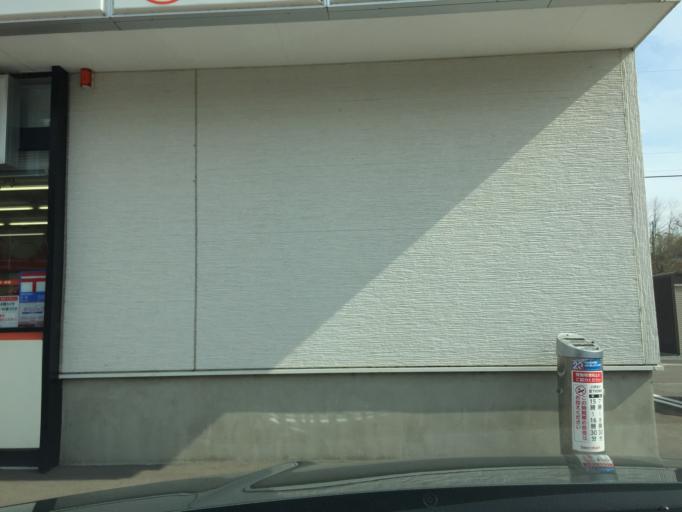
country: JP
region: Hokkaido
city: Utashinai
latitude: 43.5205
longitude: 142.0469
